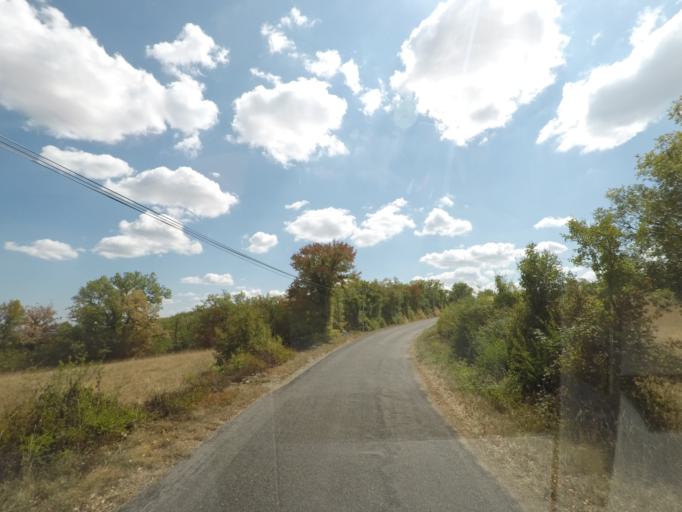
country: FR
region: Midi-Pyrenees
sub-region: Departement du Lot
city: Cajarc
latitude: 44.5353
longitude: 1.6643
